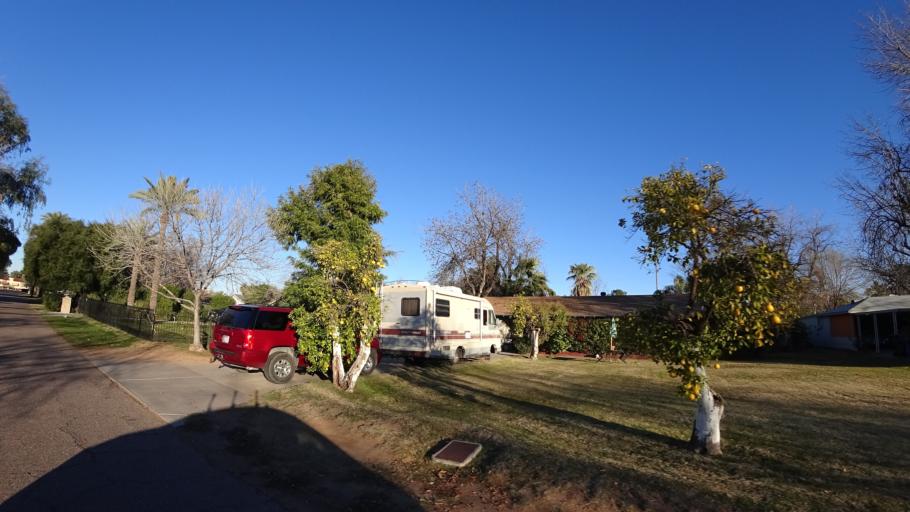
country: US
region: Arizona
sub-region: Maricopa County
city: Phoenix
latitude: 33.4891
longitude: -112.0101
